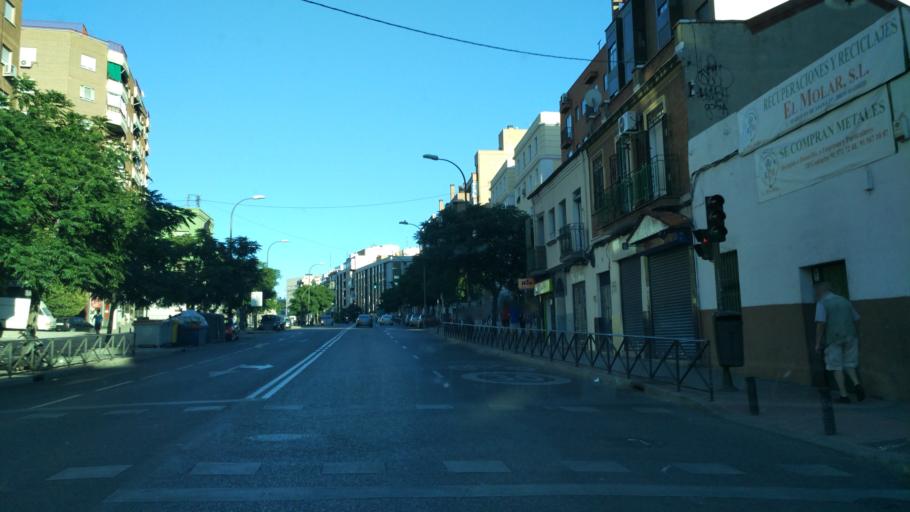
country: ES
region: Madrid
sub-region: Provincia de Madrid
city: Tetuan de las Victorias
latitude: 40.4617
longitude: -3.7006
